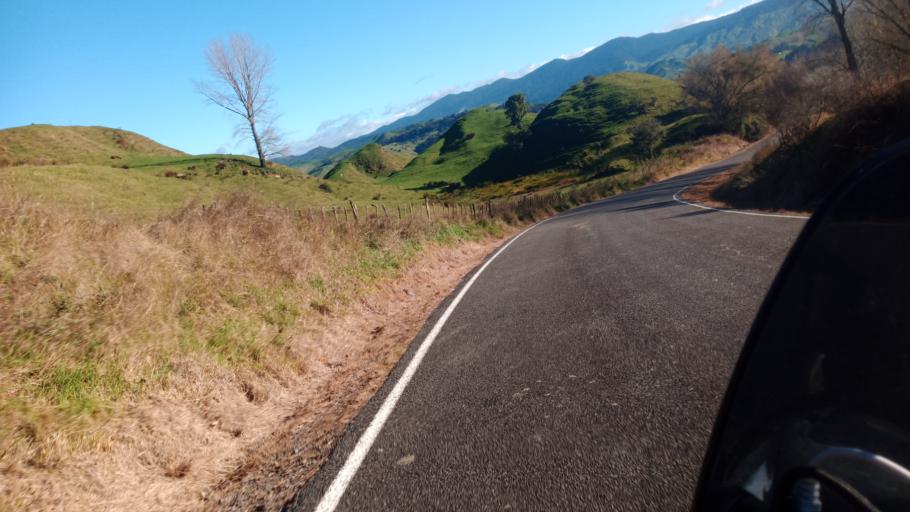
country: NZ
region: Hawke's Bay
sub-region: Wairoa District
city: Wairoa
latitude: -38.8250
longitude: 177.2910
